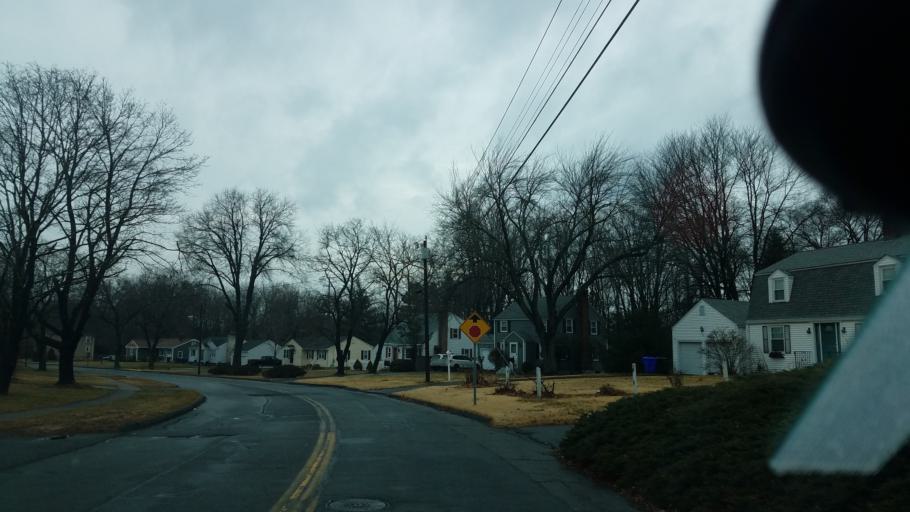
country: US
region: Connecticut
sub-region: Hartford County
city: East Hartford
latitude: 41.7705
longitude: -72.5948
